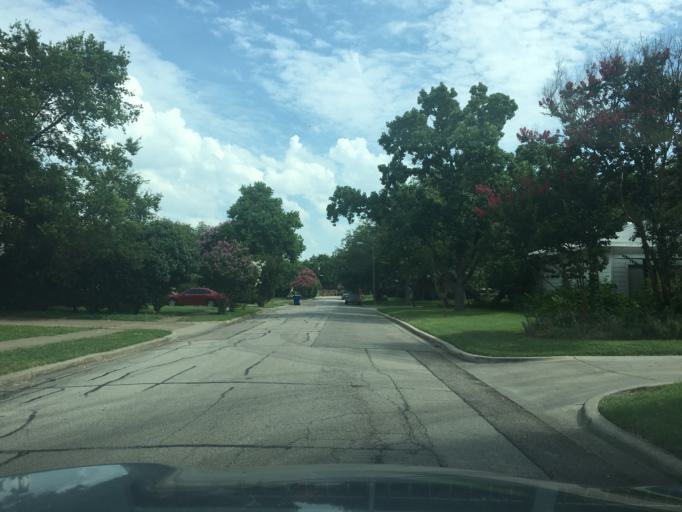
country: US
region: Texas
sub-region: Dallas County
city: Farmers Branch
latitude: 32.9280
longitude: -96.8651
